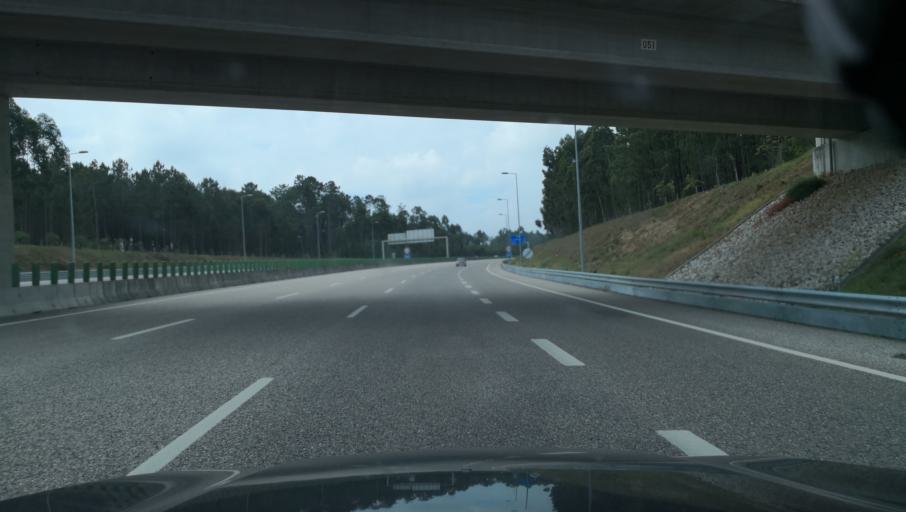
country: PT
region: Leiria
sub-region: Pombal
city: Lourical
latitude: 39.9420
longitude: -8.7701
